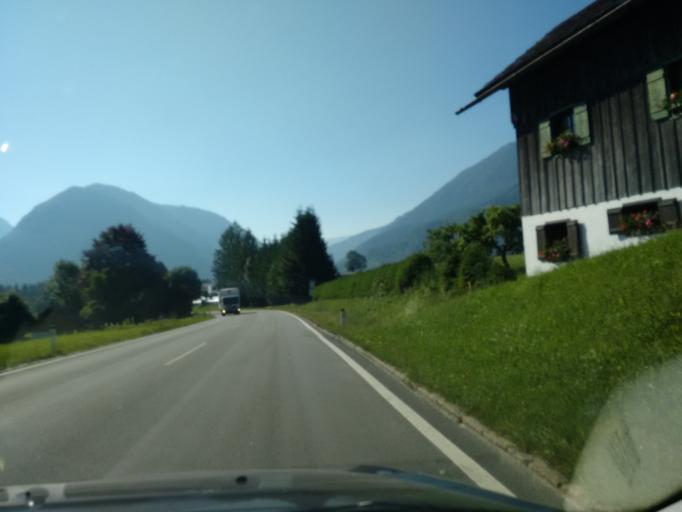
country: AT
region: Styria
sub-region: Politischer Bezirk Liezen
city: Bad Aussee
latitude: 47.6117
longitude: 13.7687
